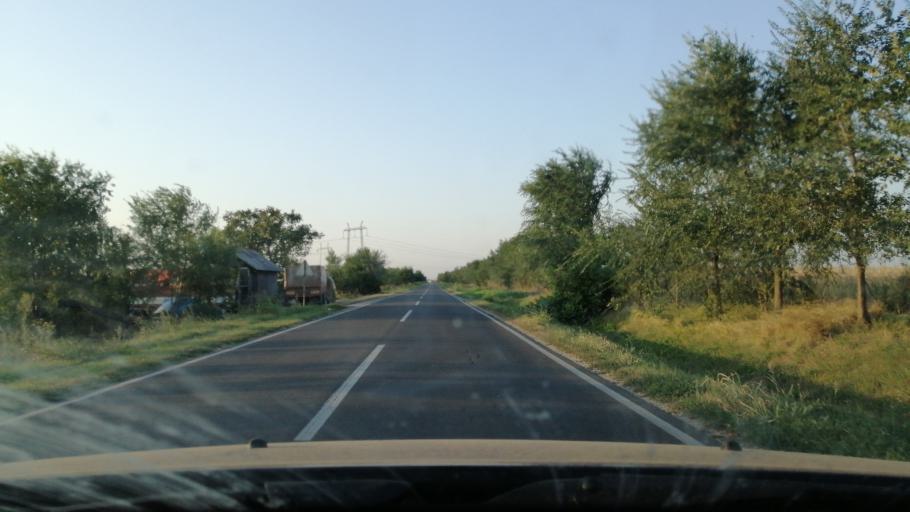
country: RS
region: Central Serbia
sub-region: Belgrade
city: Grocka
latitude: 44.7829
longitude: 20.7235
